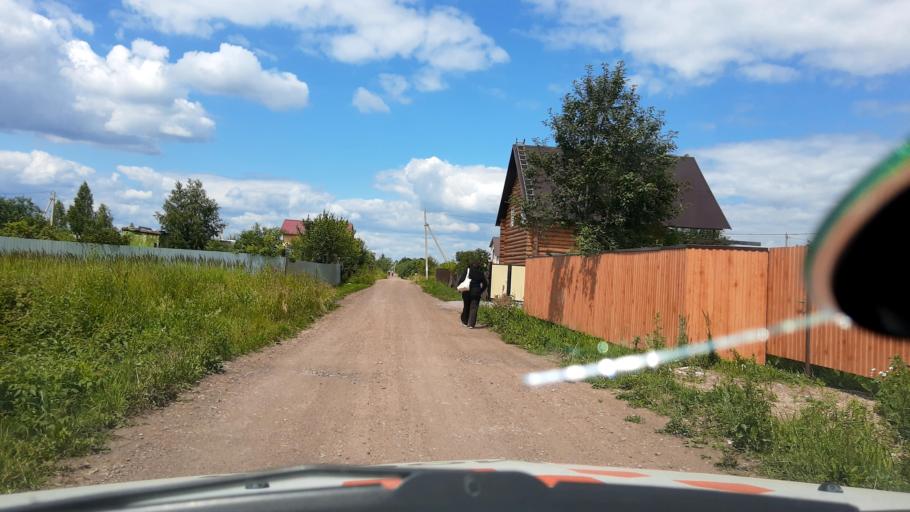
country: RU
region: Bashkortostan
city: Kabakovo
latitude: 54.7209
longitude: 56.2083
